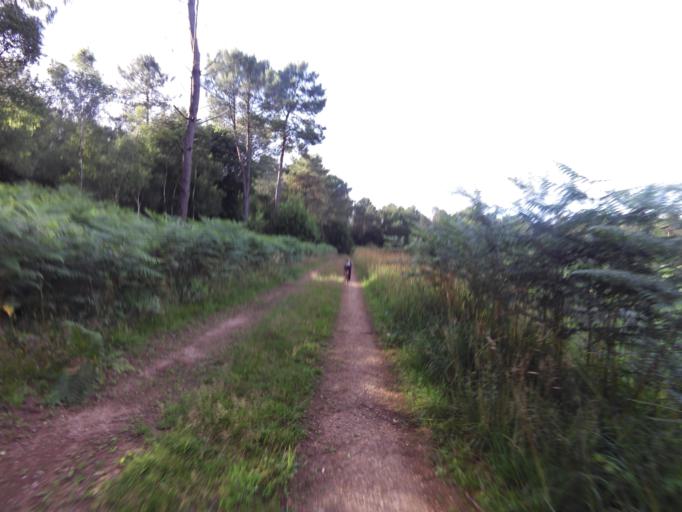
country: FR
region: Brittany
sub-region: Departement du Morbihan
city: Molac
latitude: 47.7361
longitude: -2.4179
